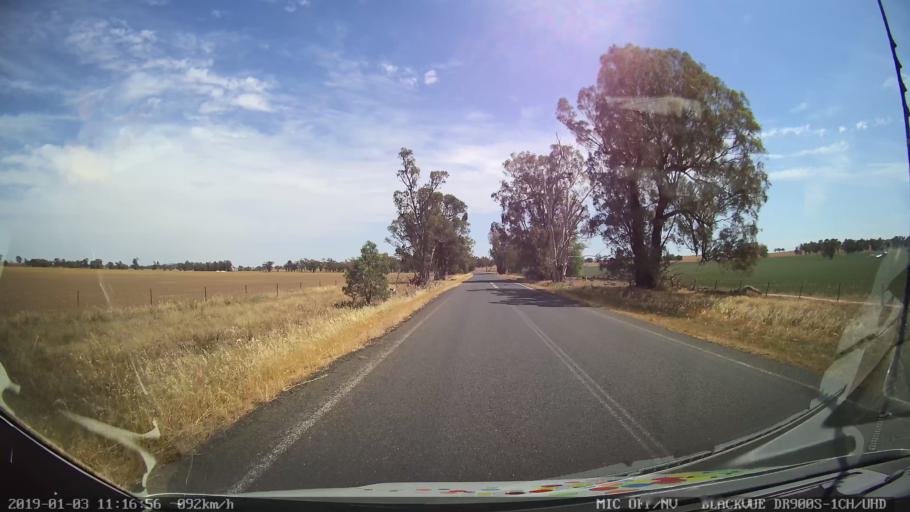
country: AU
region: New South Wales
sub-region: Young
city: Young
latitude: -34.1452
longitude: 148.2679
